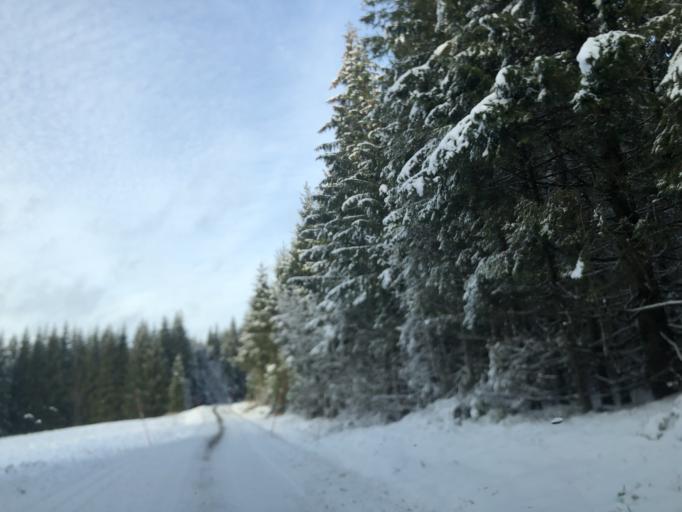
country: SE
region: Vaestra Goetaland
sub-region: Ulricehamns Kommun
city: Ulricehamn
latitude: 57.7475
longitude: 13.5077
